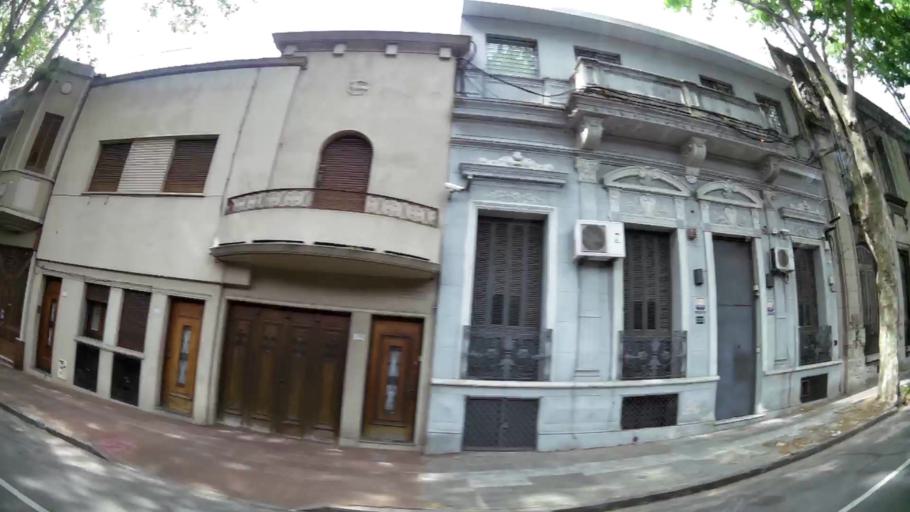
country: UY
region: Montevideo
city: Montevideo
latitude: -34.9080
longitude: -56.1681
